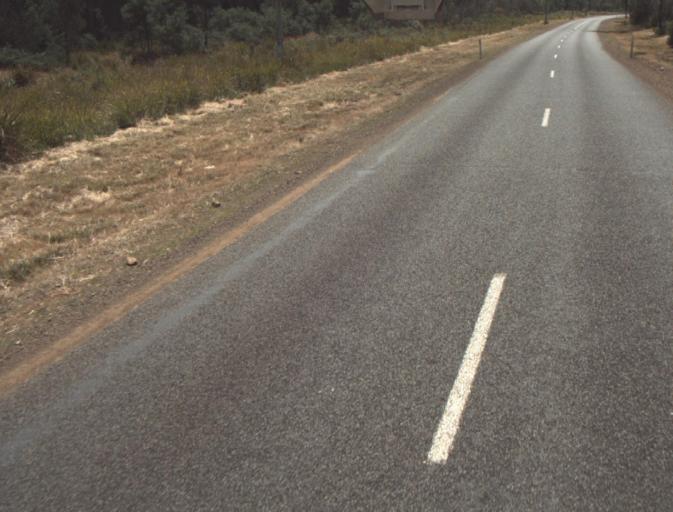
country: AU
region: Tasmania
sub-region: Launceston
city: Mayfield
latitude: -41.3115
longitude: 147.1343
